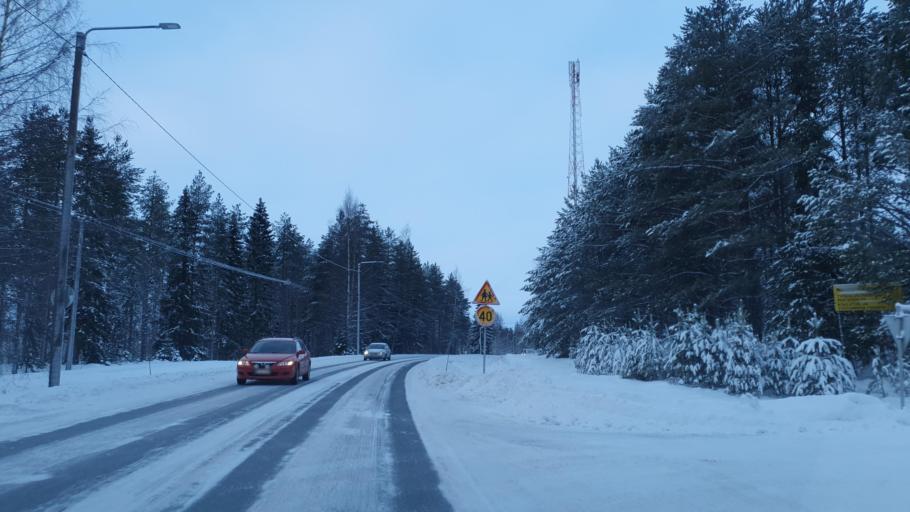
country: FI
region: Northern Ostrobothnia
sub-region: Oulu
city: Haukipudas
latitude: 65.2081
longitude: 25.3251
